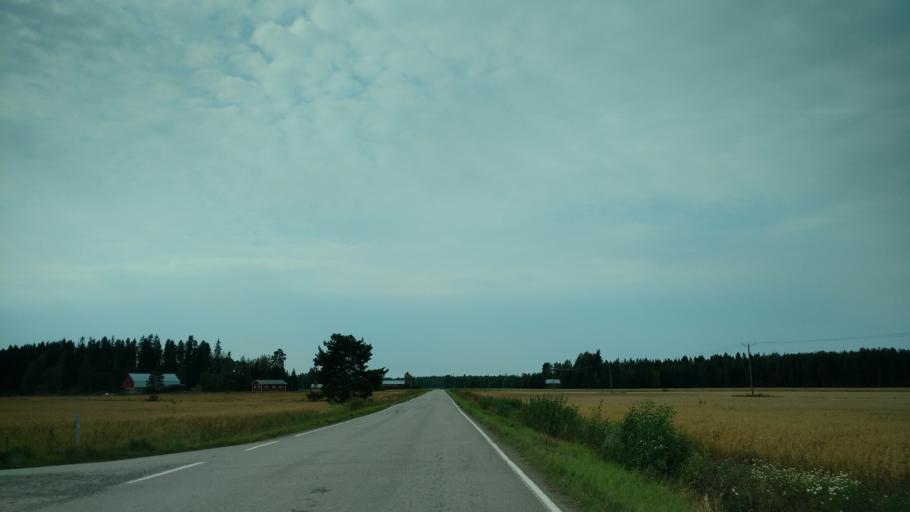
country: FI
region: Varsinais-Suomi
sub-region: Loimaa
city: Koski Tl
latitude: 60.7234
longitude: 23.1783
